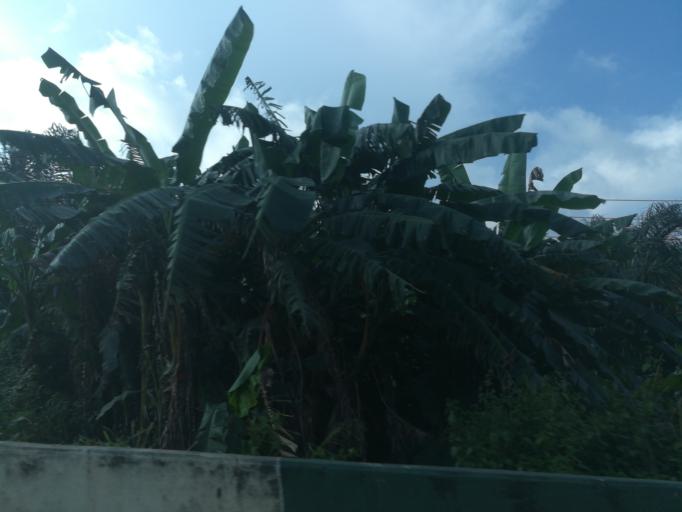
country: NG
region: Ogun
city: Ado Odo
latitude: 6.4918
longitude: 3.0782
